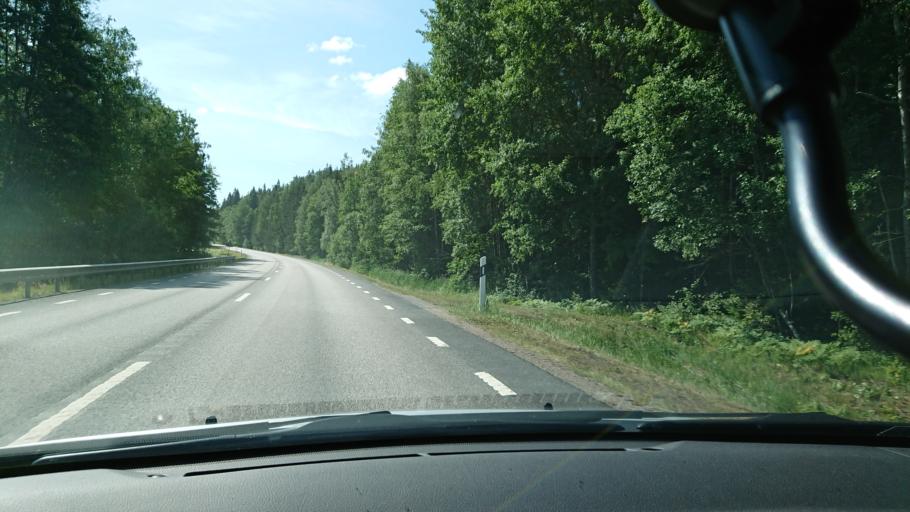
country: SE
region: OEstergoetland
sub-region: Kinda Kommun
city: Kisa
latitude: 57.9556
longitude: 15.6604
